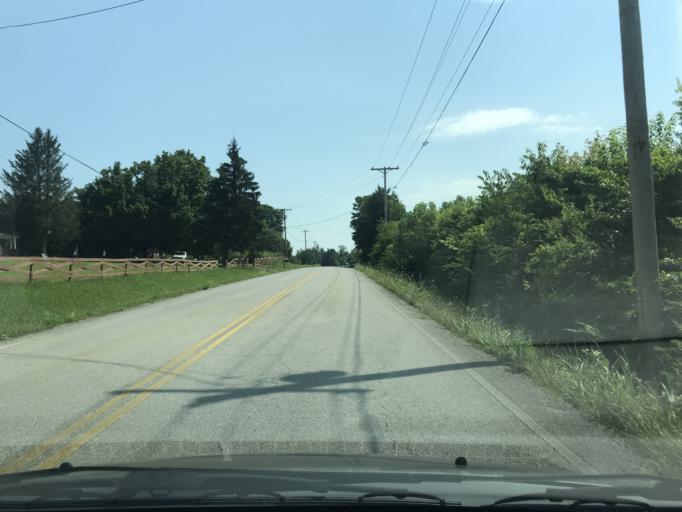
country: US
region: Tennessee
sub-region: Loudon County
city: Lenoir City
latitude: 35.8223
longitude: -84.3276
